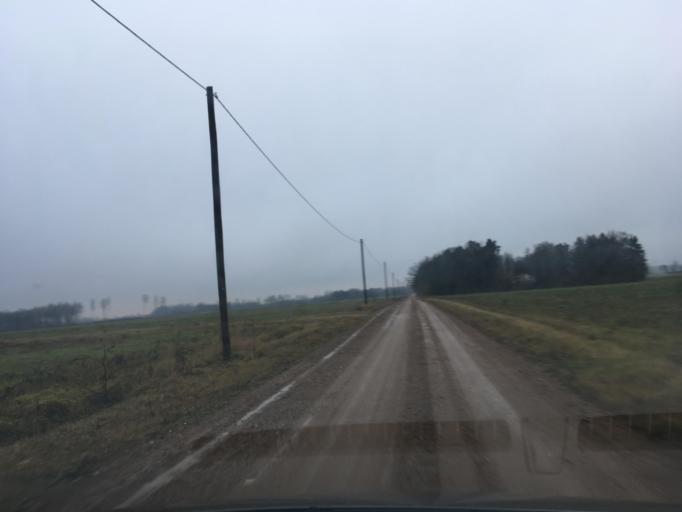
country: EE
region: Tartu
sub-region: Tartu linn
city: Tartu
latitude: 58.3814
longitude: 26.9267
